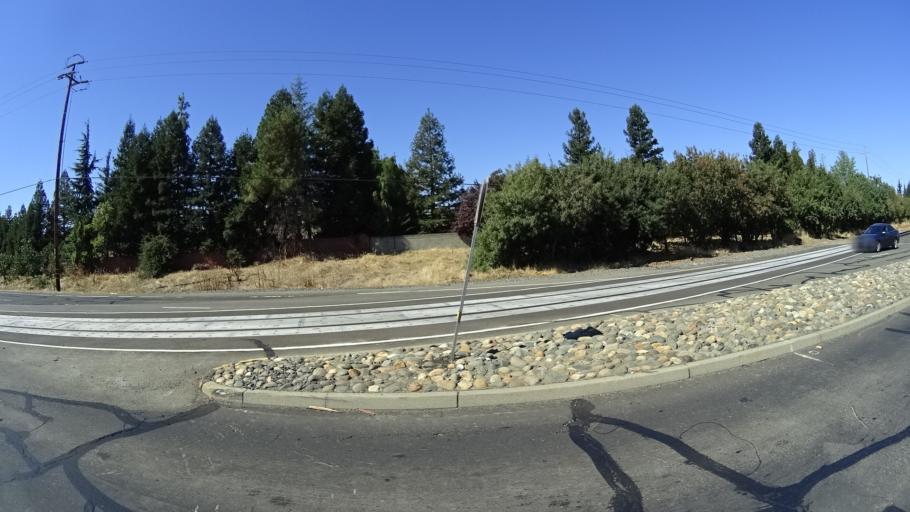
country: US
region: California
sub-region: Sacramento County
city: Elk Grove
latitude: 38.4284
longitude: -121.3716
